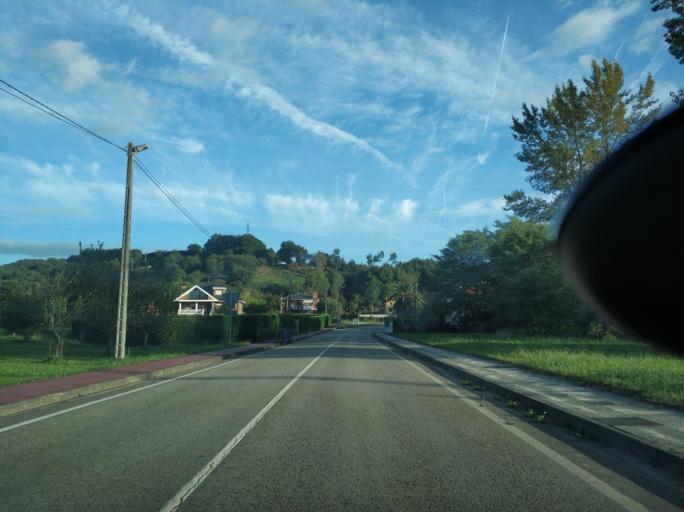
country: ES
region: Cantabria
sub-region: Provincia de Cantabria
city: Miengo
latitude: 43.4041
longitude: -3.9515
